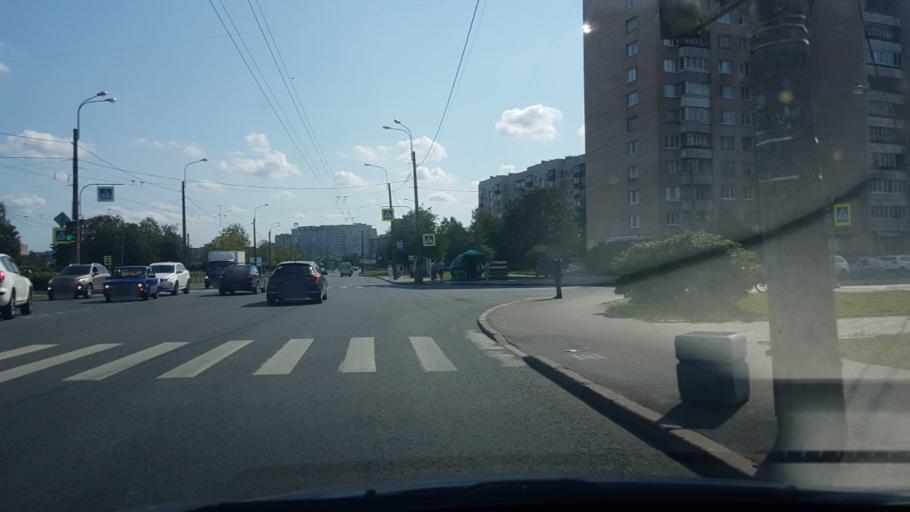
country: RU
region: St.-Petersburg
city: Sosnovaya Polyana
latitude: 59.8346
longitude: 30.1560
